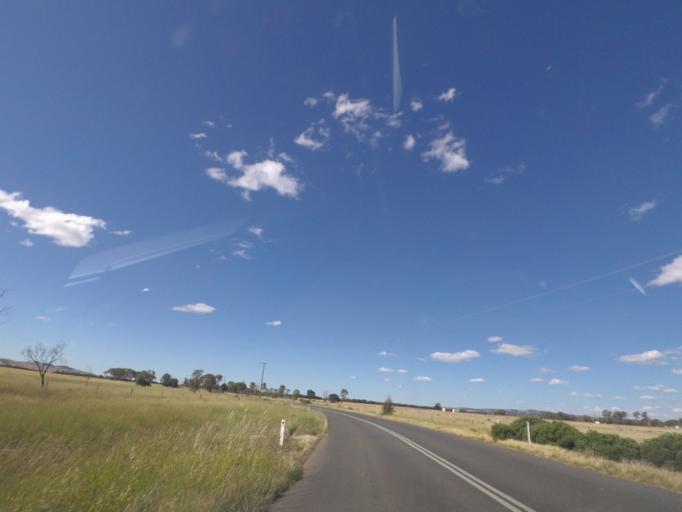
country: AU
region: Victoria
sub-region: Hume
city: Craigieburn
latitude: -37.4266
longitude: 144.8736
